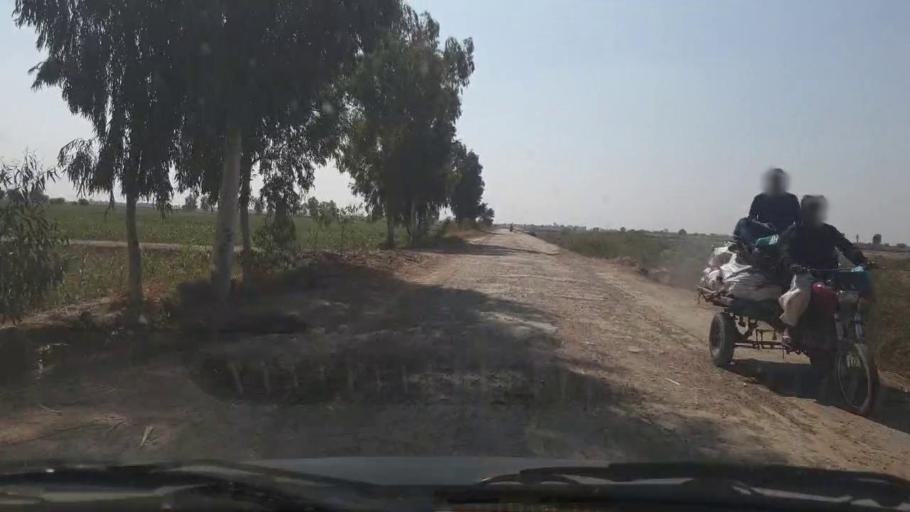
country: PK
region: Sindh
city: Samaro
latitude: 25.2440
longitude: 69.3432
